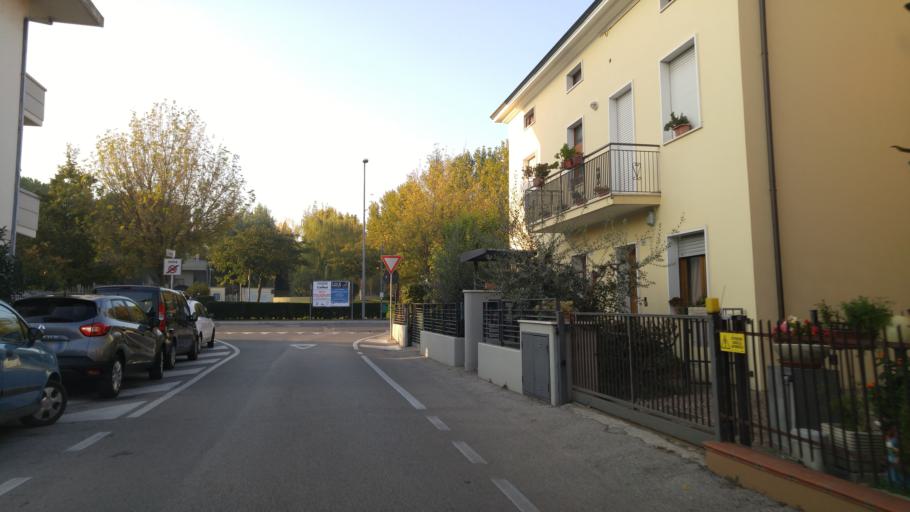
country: IT
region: The Marches
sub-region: Provincia di Pesaro e Urbino
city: Pesaro
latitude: 43.8969
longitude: 12.8883
